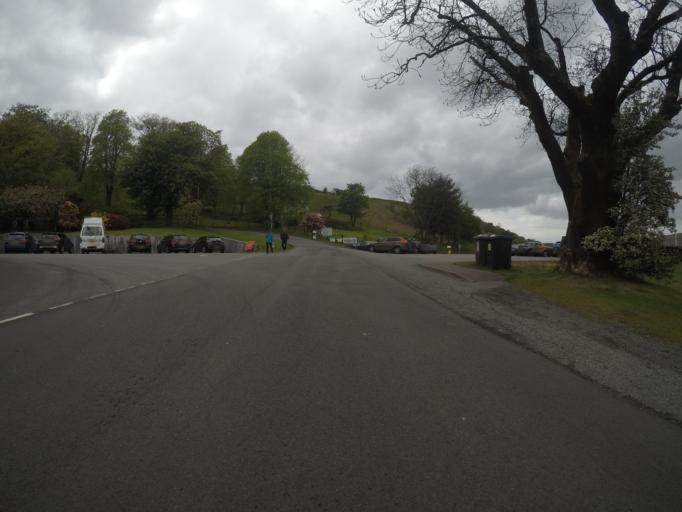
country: GB
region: Scotland
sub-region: Highland
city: Isle of Skye
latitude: 57.3030
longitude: -6.3566
